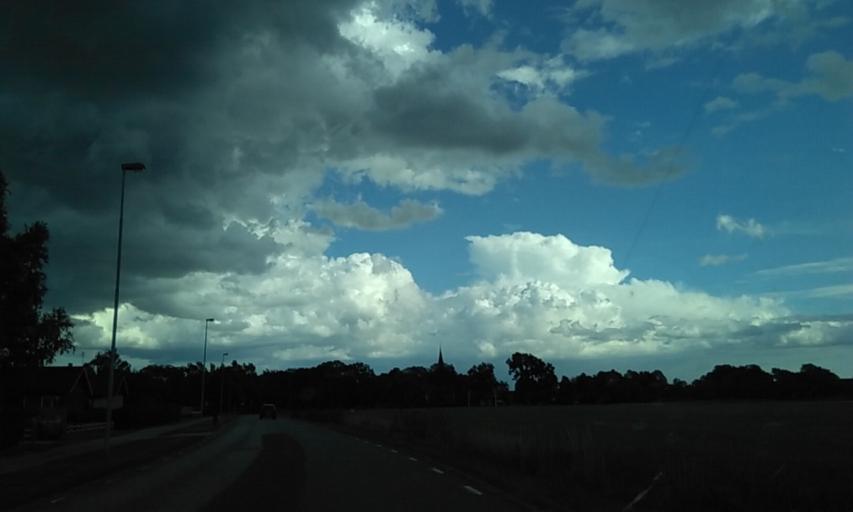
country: SE
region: Vaestra Goetaland
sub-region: Lidkopings Kommun
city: Lidkoping
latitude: 58.5109
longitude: 13.0026
